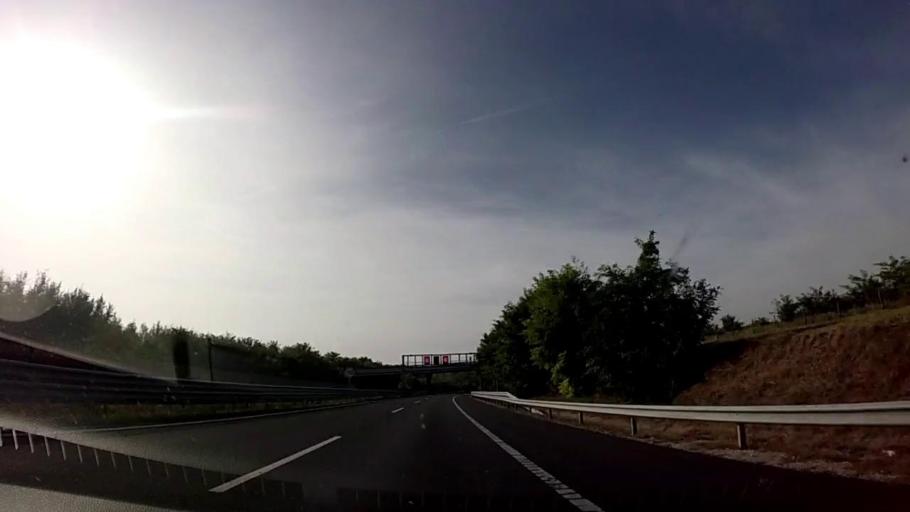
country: HU
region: Somogy
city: Balatonfoldvar
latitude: 46.8226
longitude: 17.9303
